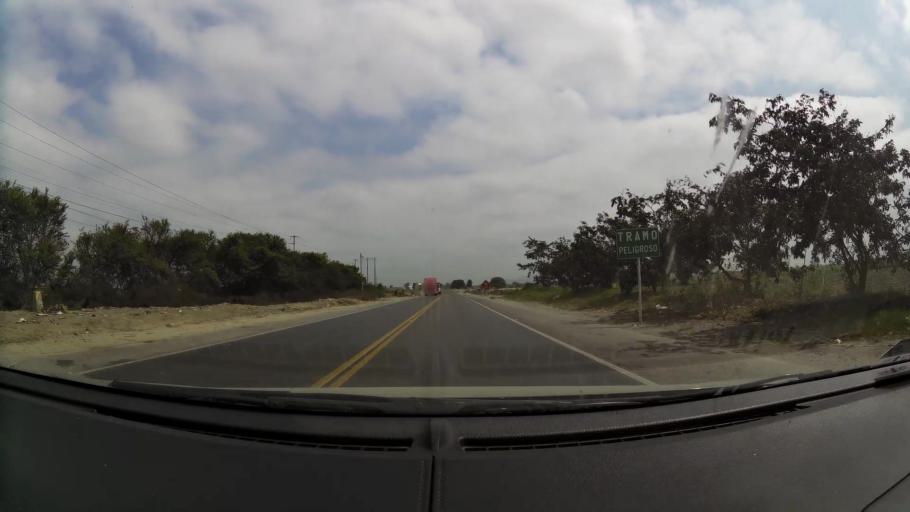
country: PE
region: La Libertad
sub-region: Ascope
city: Chicama
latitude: -7.8157
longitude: -79.1775
